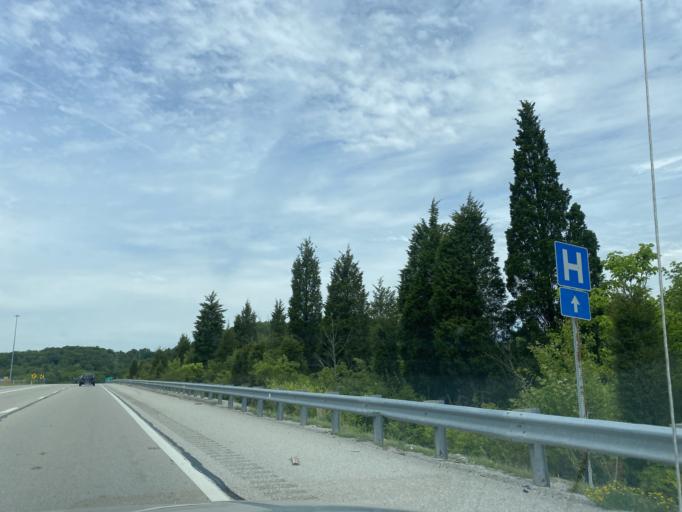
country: US
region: Kentucky
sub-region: Campbell County
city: Highland Heights
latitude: 39.0493
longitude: -84.4619
